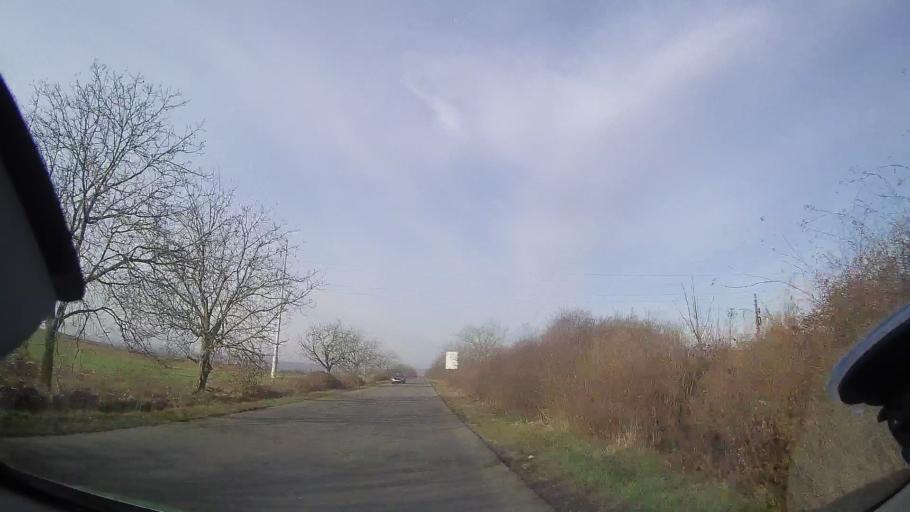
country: RO
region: Bihor
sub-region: Comuna Spinus
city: Spinus
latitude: 47.2204
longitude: 22.1720
